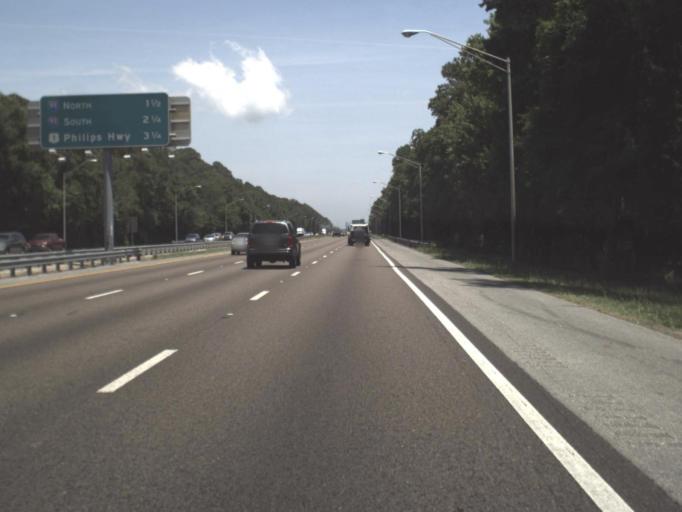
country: US
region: Florida
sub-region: Saint Johns County
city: Fruit Cove
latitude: 30.1684
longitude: -81.5927
